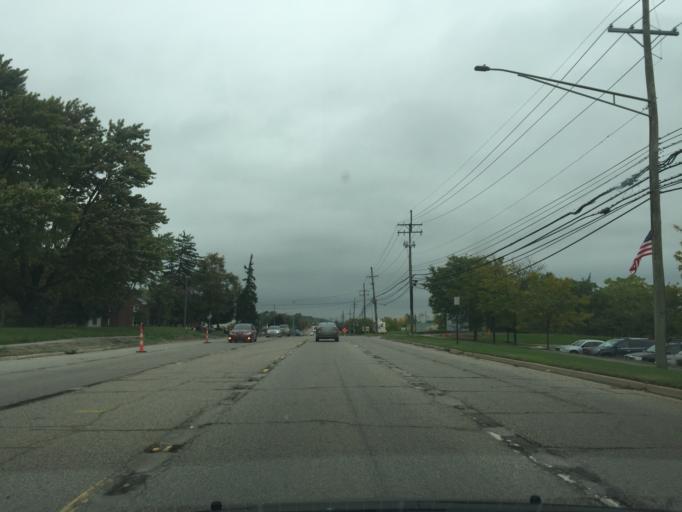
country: US
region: Michigan
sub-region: Oakland County
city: Auburn Hills
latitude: 42.6671
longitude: -83.2456
